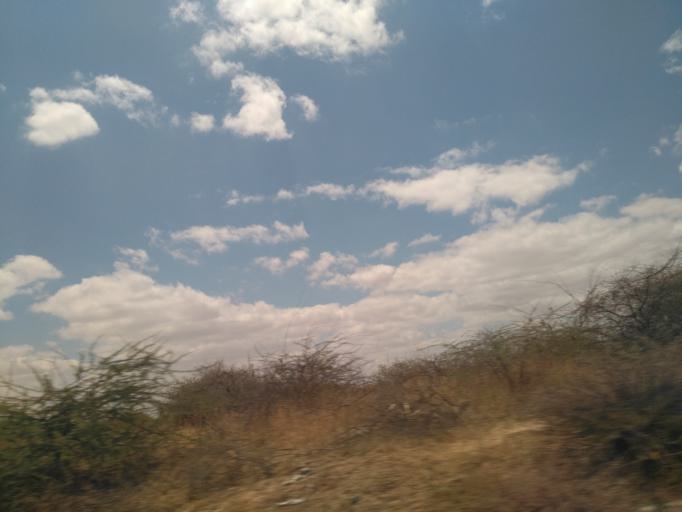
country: TZ
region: Dodoma
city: Kisasa
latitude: -6.1739
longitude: 35.7891
